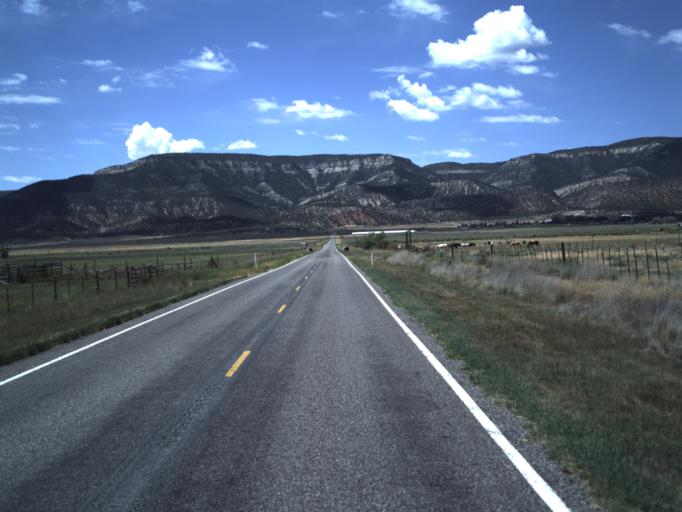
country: US
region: Utah
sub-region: Sanpete County
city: Moroni
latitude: 39.4756
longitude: -111.6053
